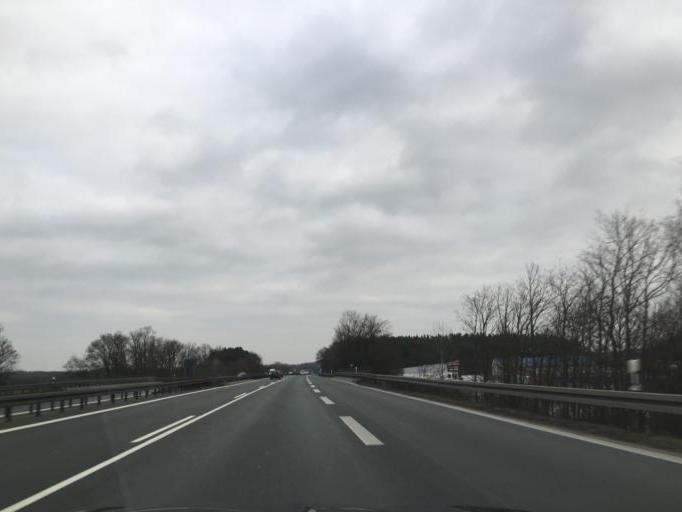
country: DE
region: Bavaria
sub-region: Regierungsbezirk Mittelfranken
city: Gremsdorf
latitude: 49.6998
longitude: 10.8550
